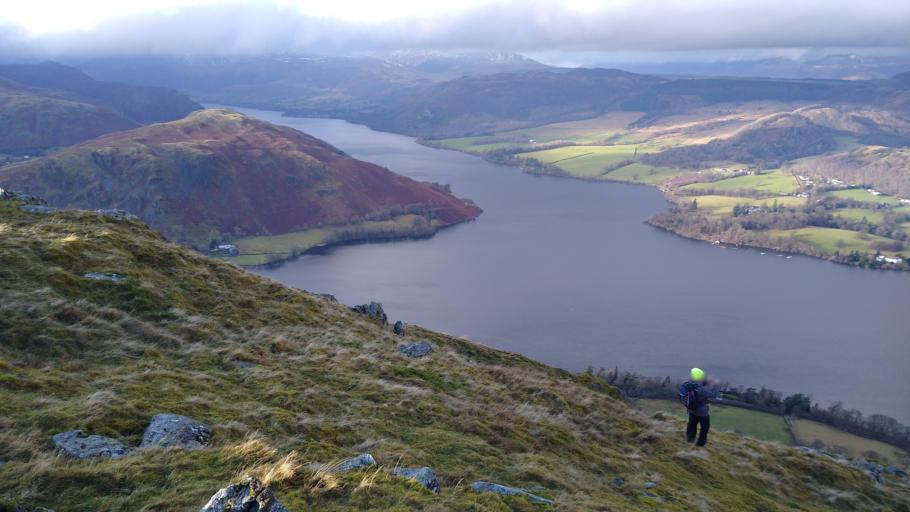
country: GB
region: England
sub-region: Cumbria
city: Penrith
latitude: 54.5735
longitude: -2.8464
